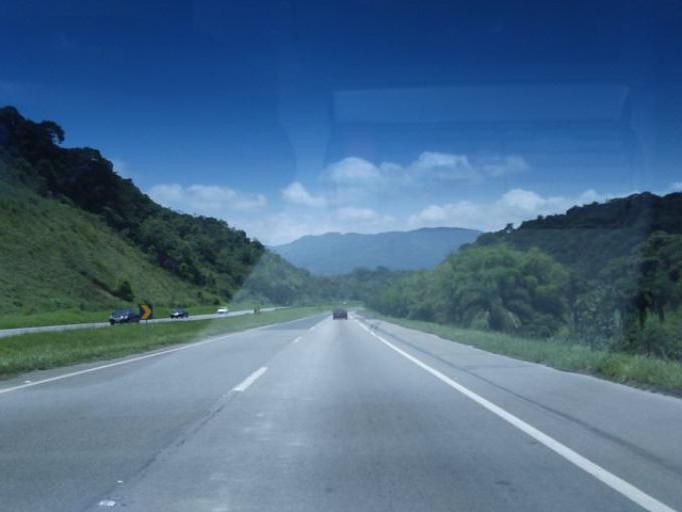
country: BR
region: Sao Paulo
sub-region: Miracatu
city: Miracatu
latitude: -24.2326
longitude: -47.3605
